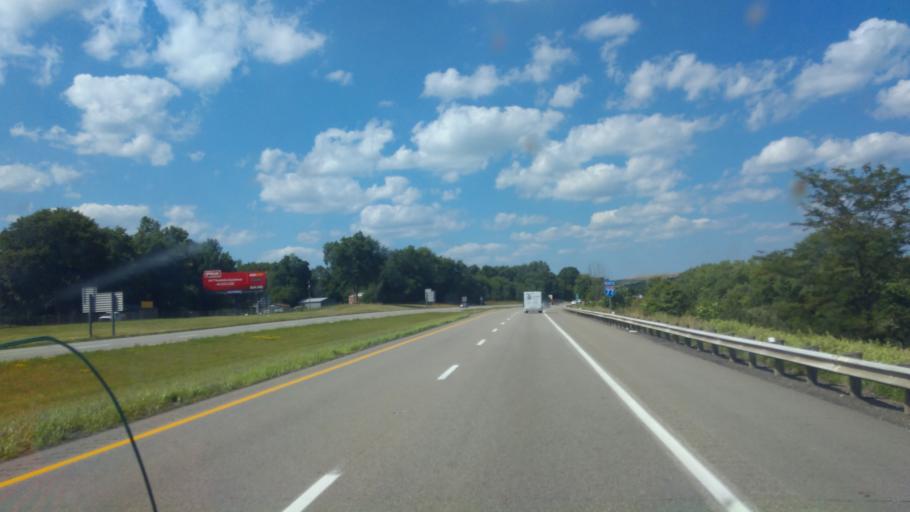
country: US
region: Ohio
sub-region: Tuscarawas County
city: Strasburg
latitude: 40.6515
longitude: -81.4490
